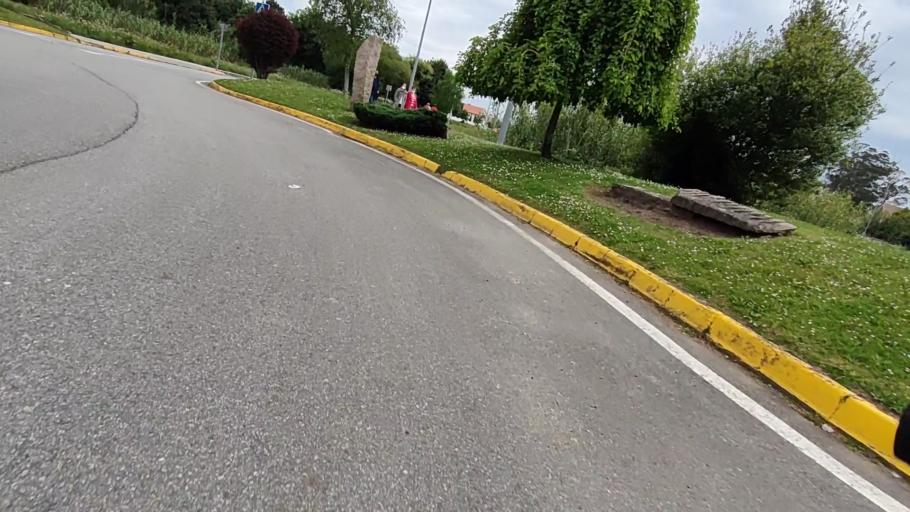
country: ES
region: Galicia
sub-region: Provincia da Coruna
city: Boiro
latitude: 42.6433
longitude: -8.8870
